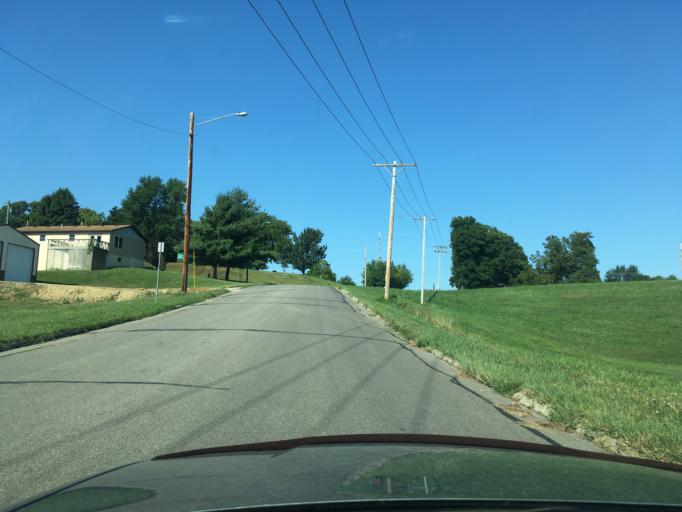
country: US
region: Kansas
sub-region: Atchison County
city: Atchison
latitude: 39.5784
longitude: -95.1220
